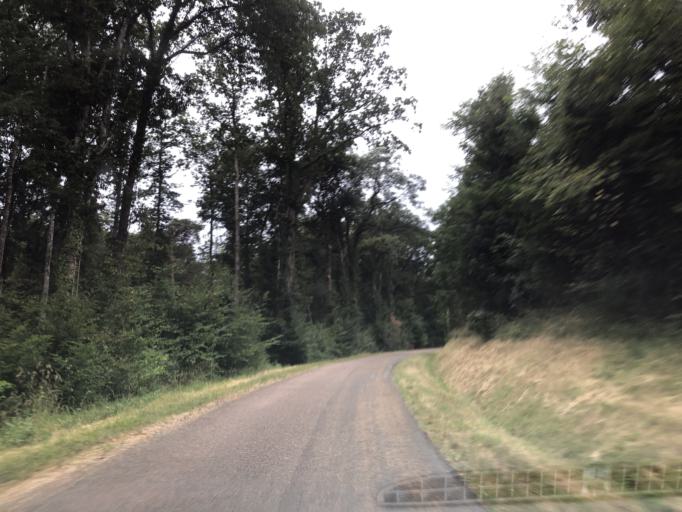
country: FR
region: Bourgogne
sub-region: Departement de l'Yonne
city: Aillant-sur-Tholon
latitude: 47.9013
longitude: 3.3171
